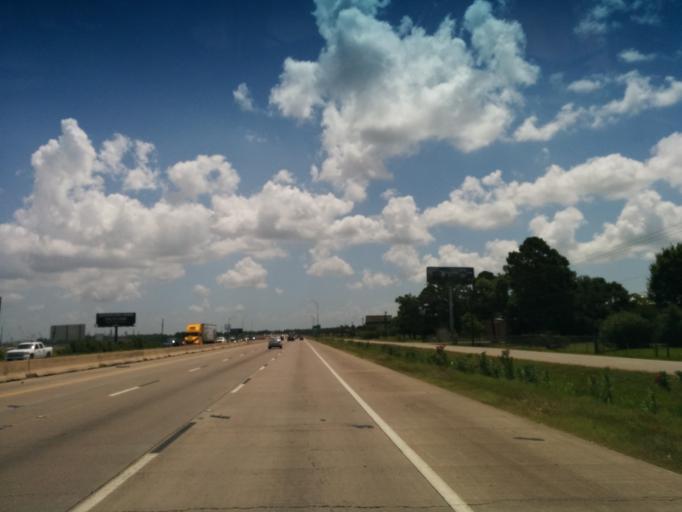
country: US
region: Texas
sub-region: Chambers County
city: Mont Belvieu
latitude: 29.8102
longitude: -94.9495
